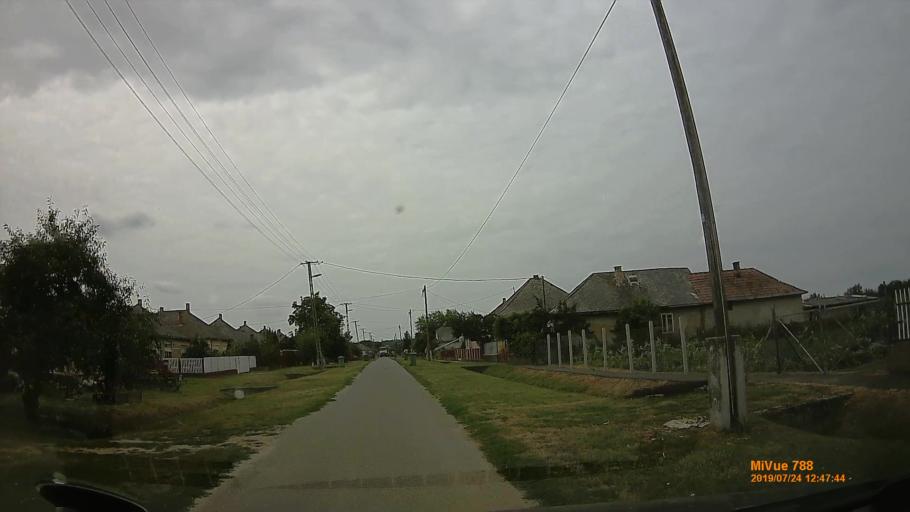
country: HU
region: Szabolcs-Szatmar-Bereg
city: Aranyosapati
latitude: 48.1922
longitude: 22.3153
